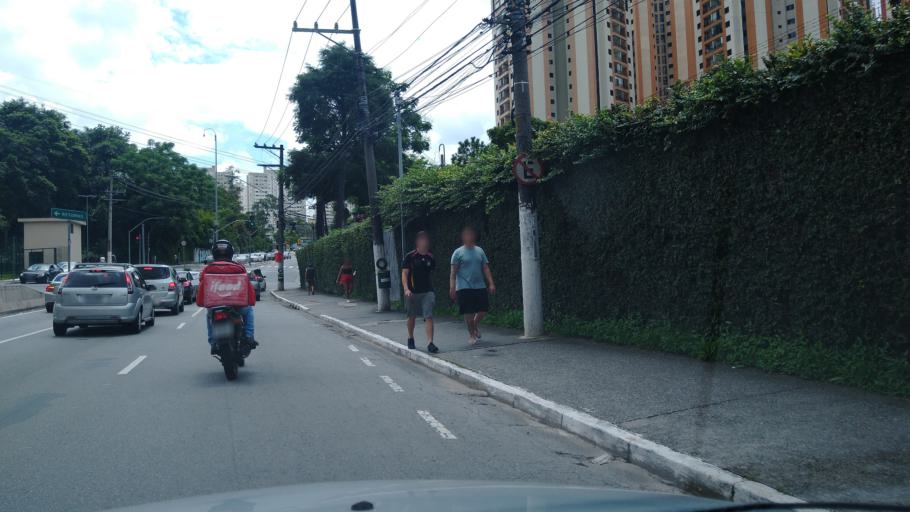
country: BR
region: Sao Paulo
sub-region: Osasco
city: Osasco
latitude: -23.5055
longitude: -46.7178
